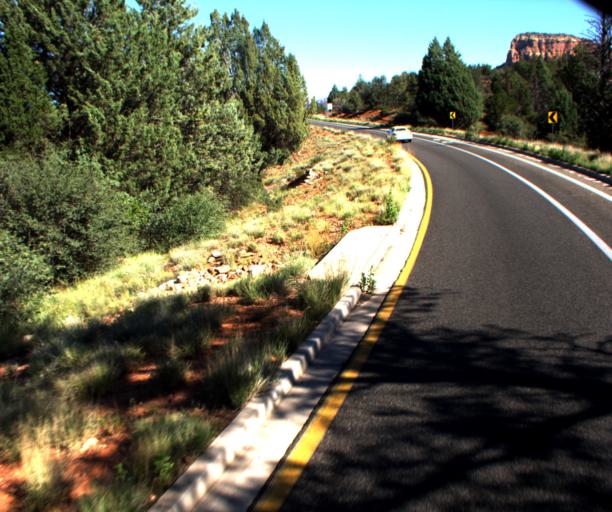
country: US
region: Arizona
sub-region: Yavapai County
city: Village of Oak Creek (Big Park)
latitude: 34.8113
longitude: -111.7647
